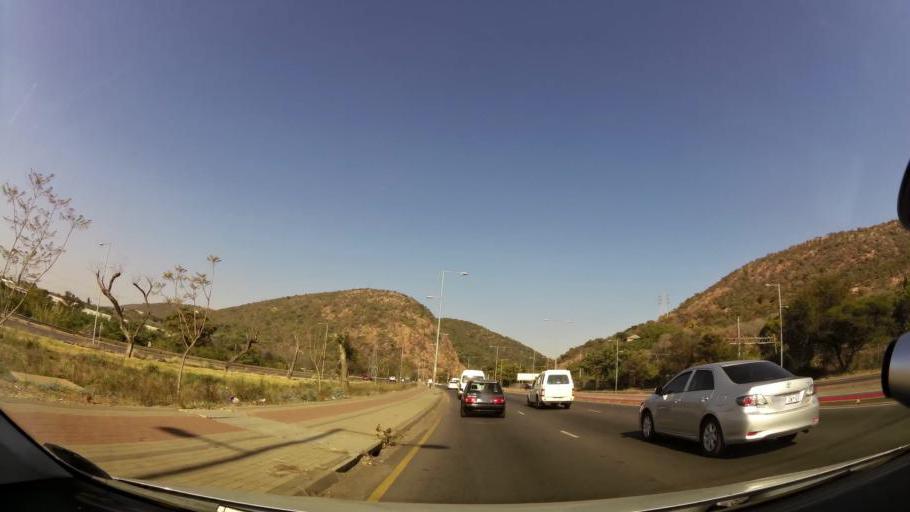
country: ZA
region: Gauteng
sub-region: City of Tshwane Metropolitan Municipality
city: Pretoria
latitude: -25.6858
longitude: 28.1848
